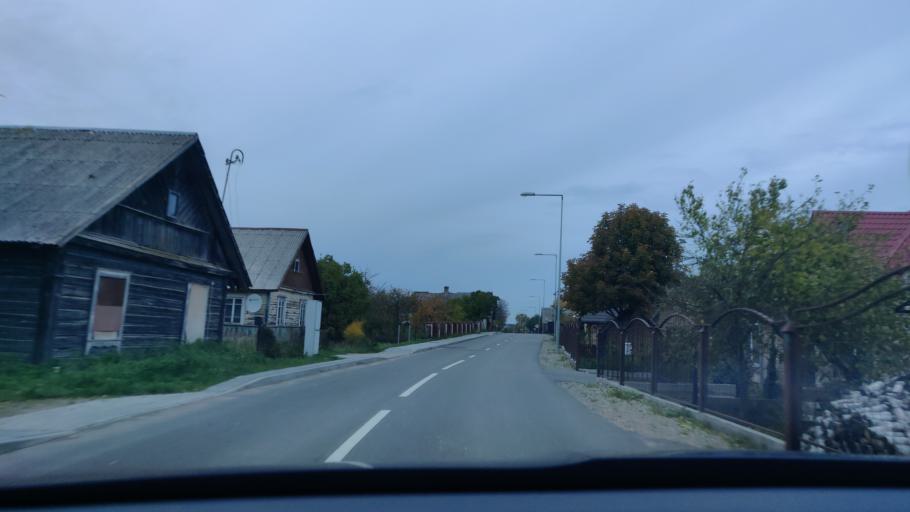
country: LT
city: Lentvaris
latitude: 54.5822
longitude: 25.0514
